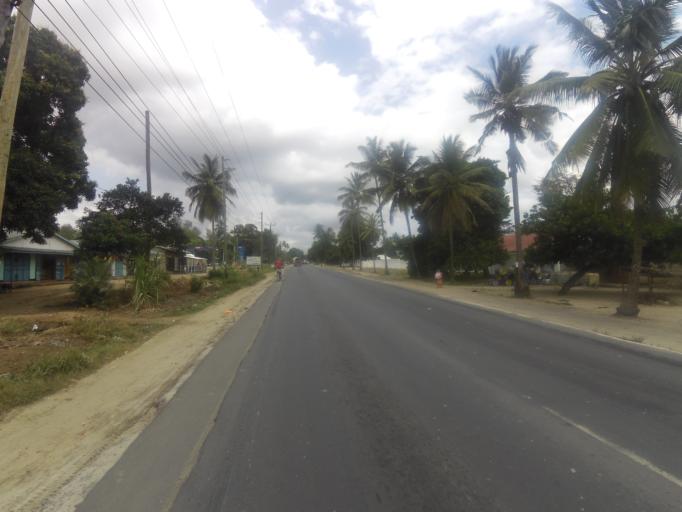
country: TZ
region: Pwani
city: Vikindu
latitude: -6.9593
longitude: 39.2843
